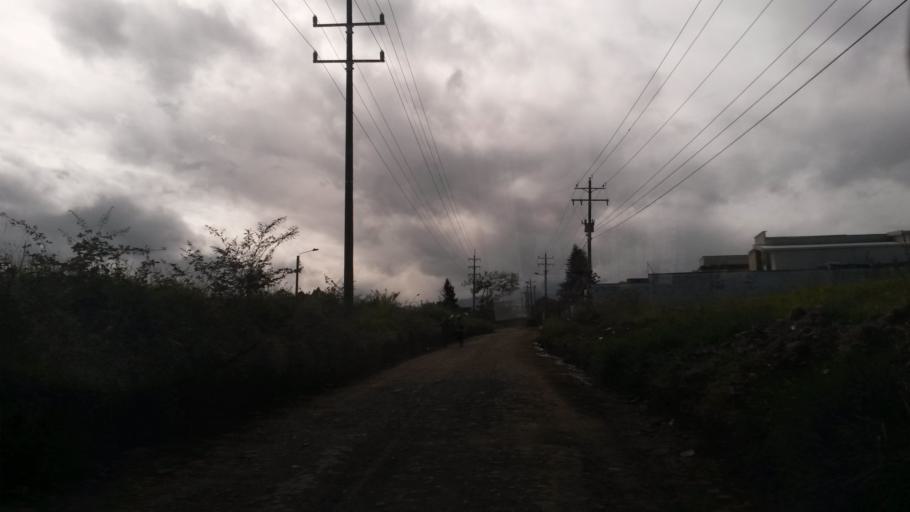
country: CO
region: Cauca
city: Popayan
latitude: 2.4808
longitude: -76.5836
